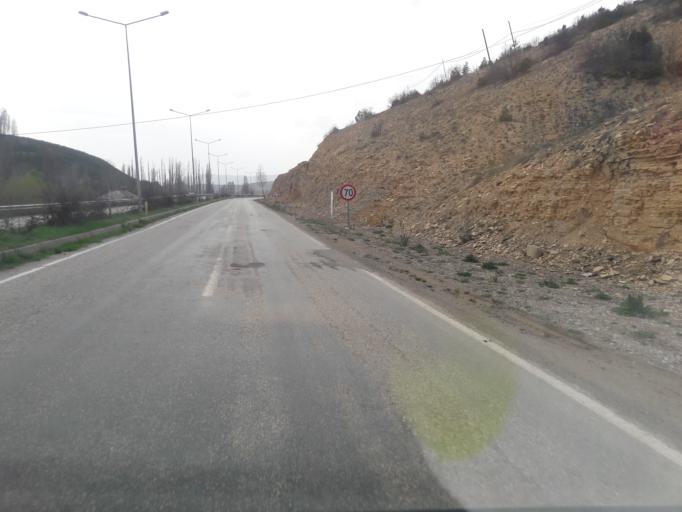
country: TR
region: Gumushane
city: Siran
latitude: 40.1765
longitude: 39.1320
